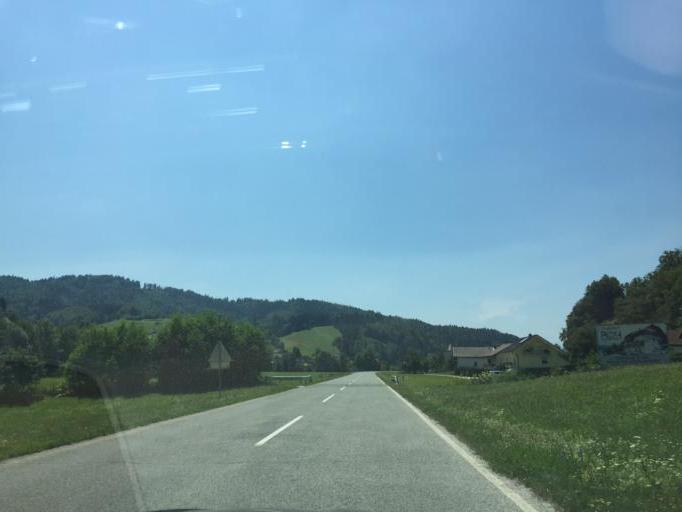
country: SI
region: Gorenja Vas-Poljane
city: Gorenja Vas
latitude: 46.1233
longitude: 14.1925
